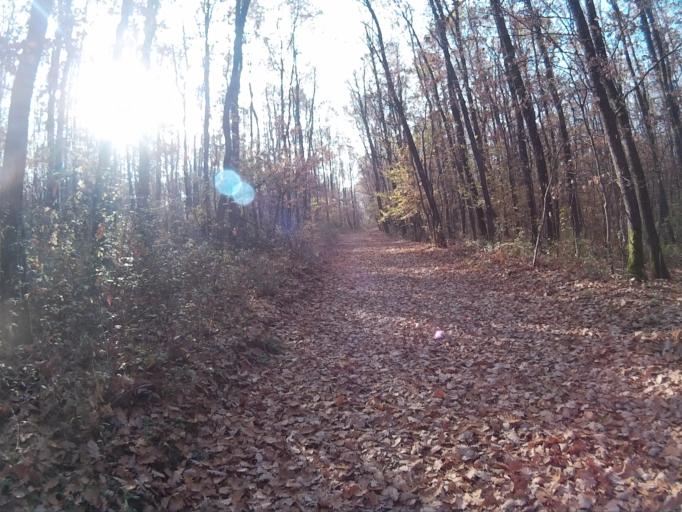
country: HU
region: Heves
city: Belapatfalva
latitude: 48.0039
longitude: 20.3832
